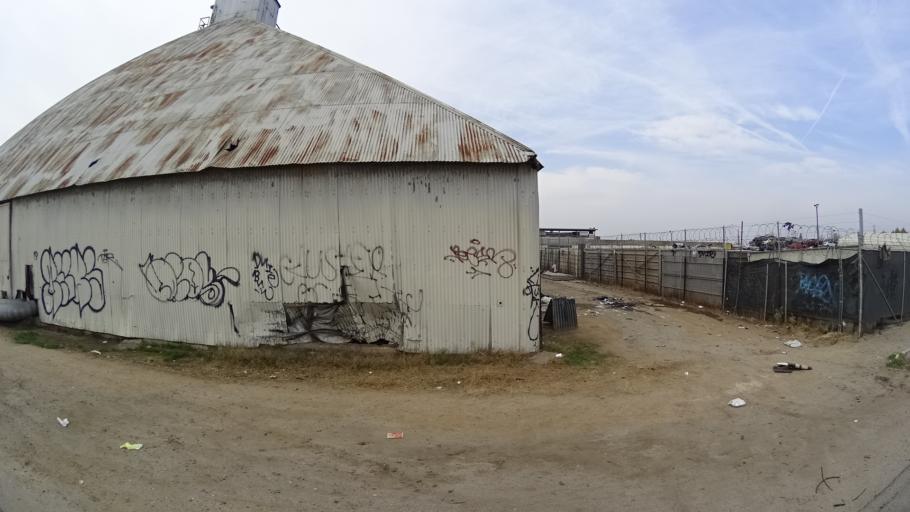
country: US
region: California
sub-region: Kern County
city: Bakersfield
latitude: 35.3708
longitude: -118.9764
